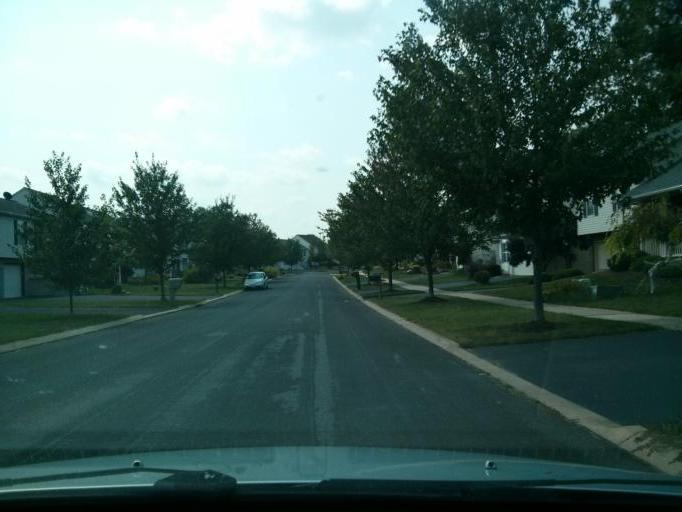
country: US
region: Pennsylvania
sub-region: Centre County
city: State College
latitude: 40.7719
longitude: -77.8774
